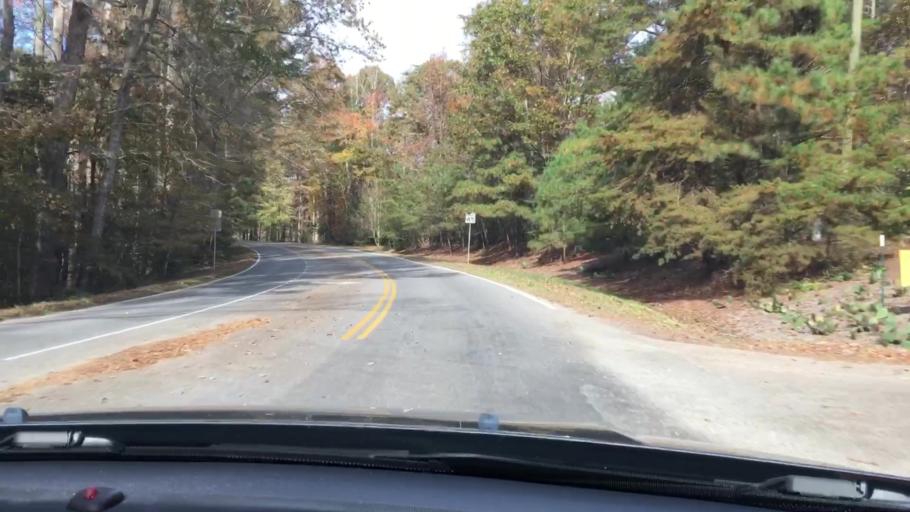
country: US
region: Virginia
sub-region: King William County
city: West Point
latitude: 37.4877
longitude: -76.8119
